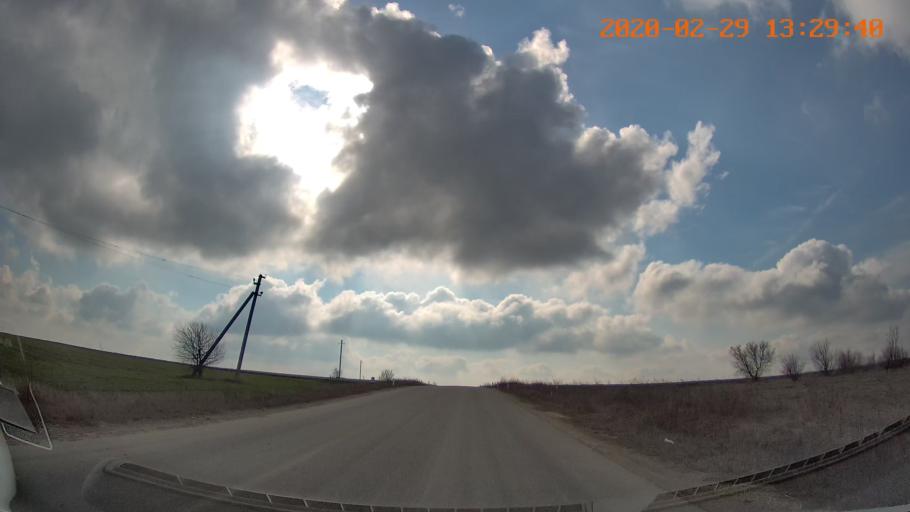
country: MD
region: Telenesti
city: Camenca
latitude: 47.8946
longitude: 28.6347
